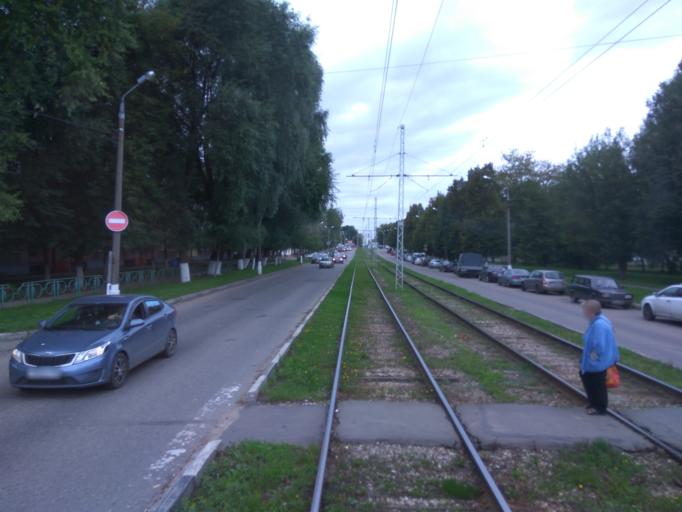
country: RU
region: Moskovskaya
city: Kolomna
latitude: 55.0794
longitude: 38.7672
